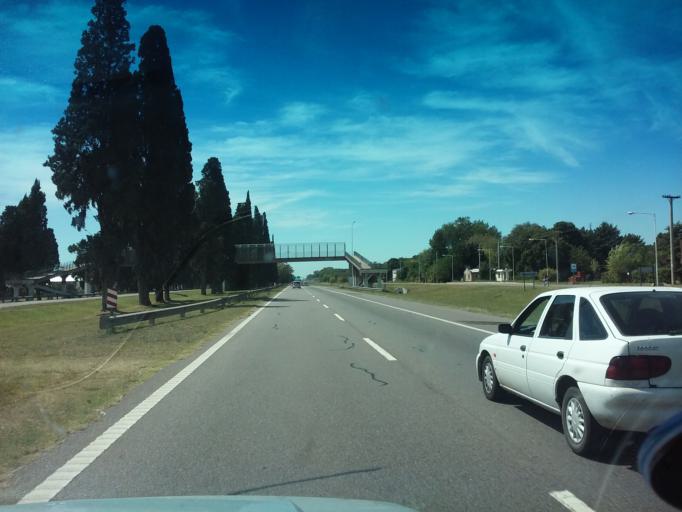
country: AR
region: Buenos Aires
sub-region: Partido de Mercedes
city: Mercedes
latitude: -34.6603
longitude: -59.3754
